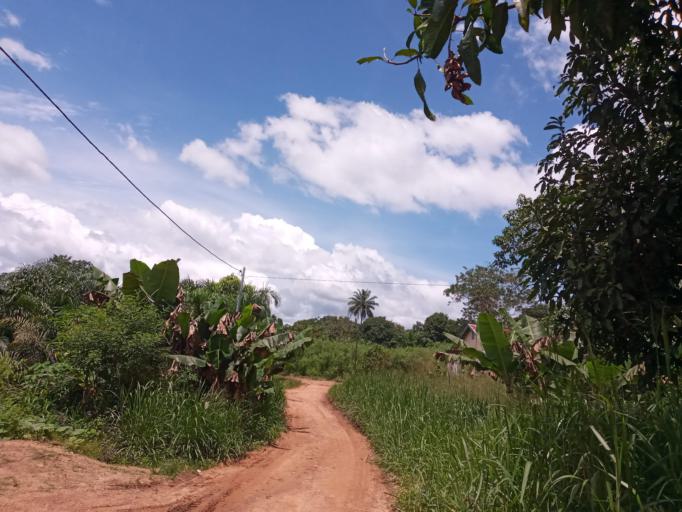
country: SL
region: Eastern Province
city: Tombu
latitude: 8.6283
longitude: -10.8232
